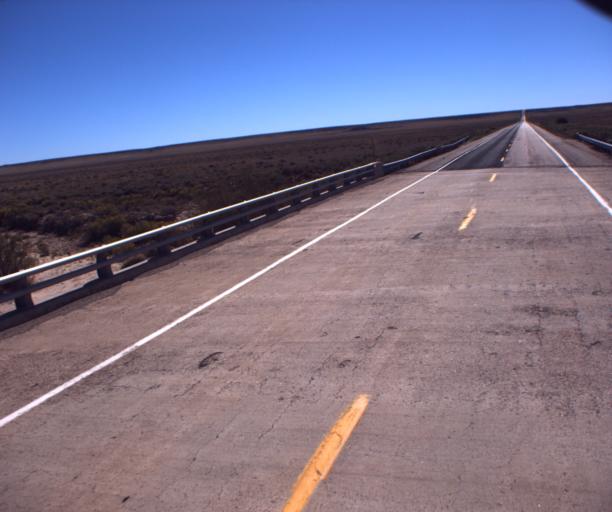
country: US
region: Arizona
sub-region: Navajo County
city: Snowflake
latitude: 34.7444
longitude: -109.7958
